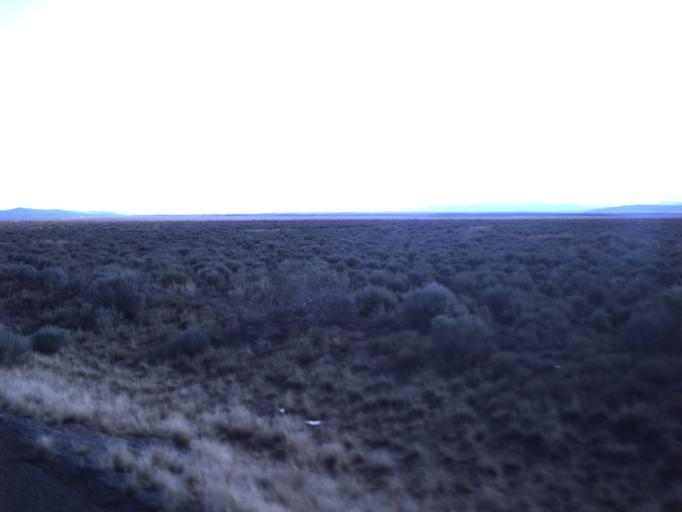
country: US
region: Utah
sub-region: Iron County
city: Enoch
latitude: 37.9193
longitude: -113.0315
